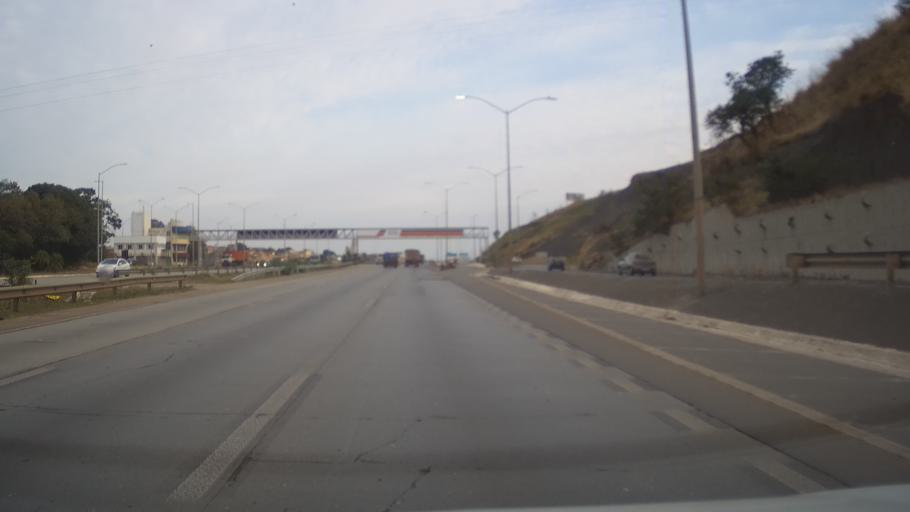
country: BR
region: Minas Gerais
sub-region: Vespasiano
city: Vespasiano
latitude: -19.7784
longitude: -43.9485
